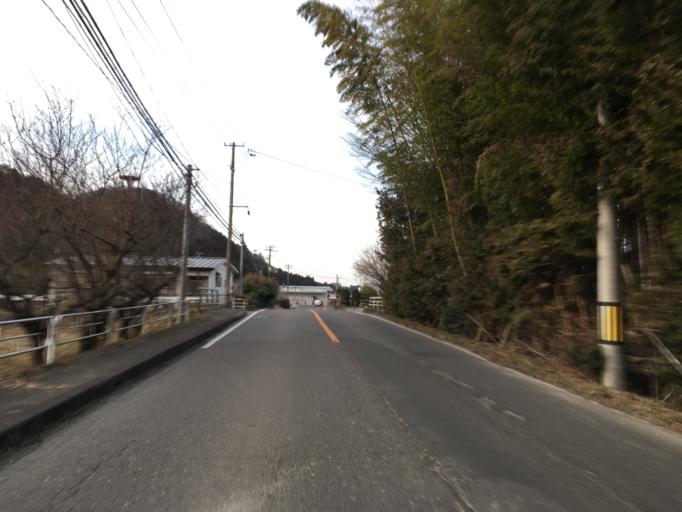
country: JP
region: Ibaraki
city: Daigo
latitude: 36.9120
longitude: 140.4081
